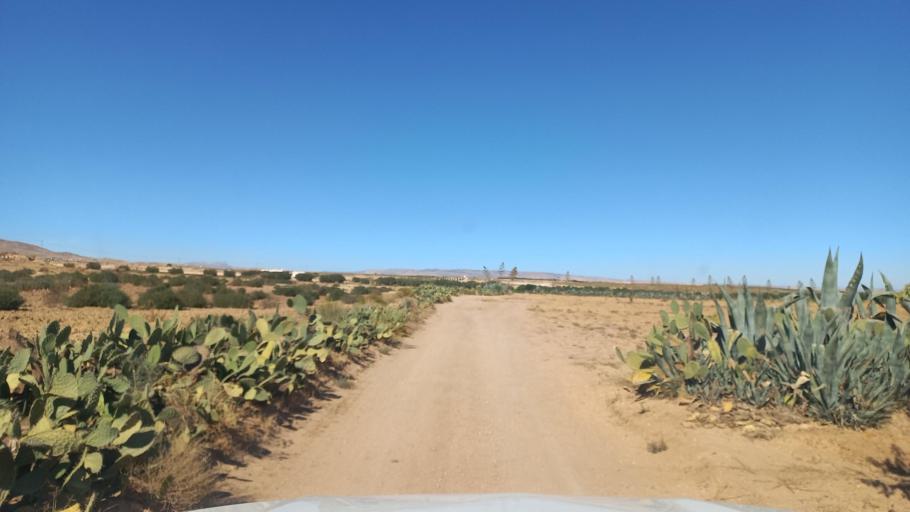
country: TN
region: Al Qasrayn
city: Sbiba
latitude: 35.4015
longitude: 9.0865
